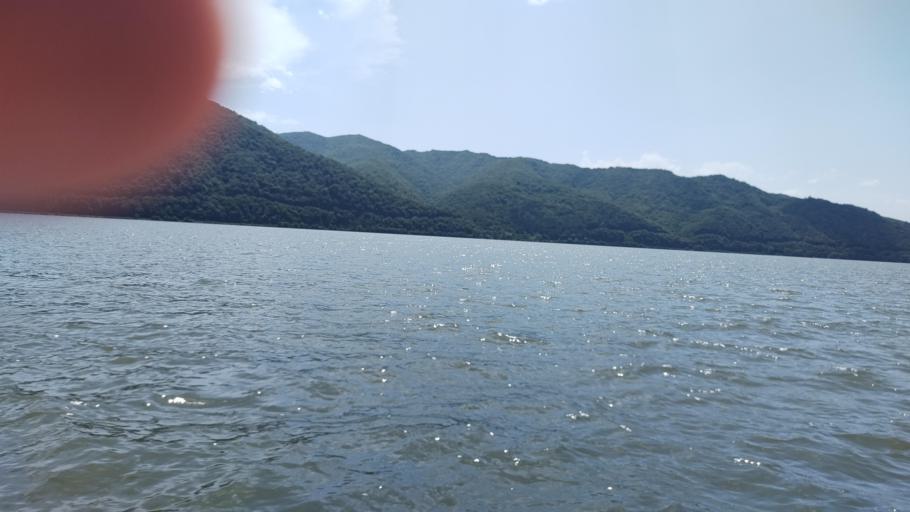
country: RO
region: Caras-Severin
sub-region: Comuna Berzasca
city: Liubcova
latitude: 44.6544
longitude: 21.8315
